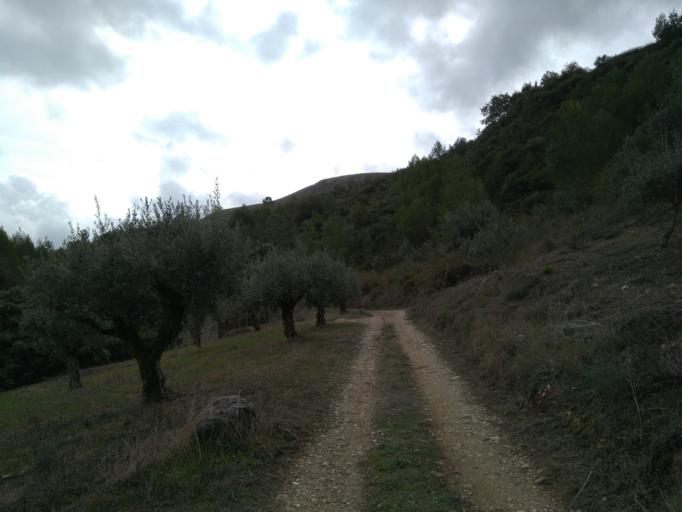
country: PT
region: Leiria
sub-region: Porto de Mos
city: Porto de Mos
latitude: 39.5819
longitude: -8.8189
